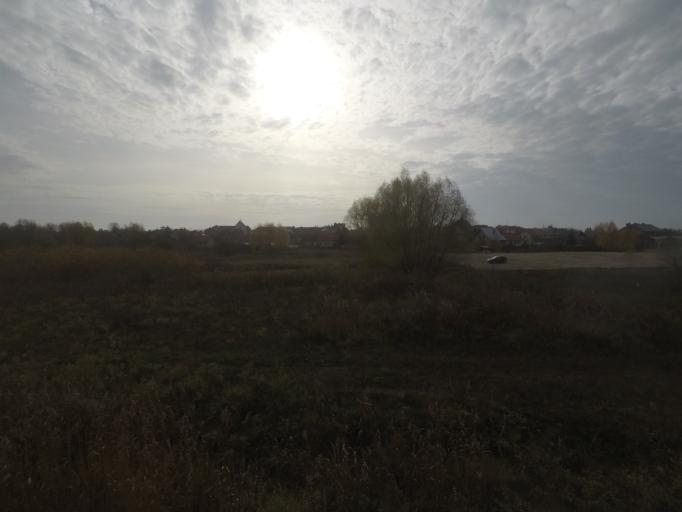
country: PL
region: Subcarpathian Voivodeship
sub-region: Powiat ropczycko-sedziszowski
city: Sedziszow Malopolski
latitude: 50.0748
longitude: 21.7036
